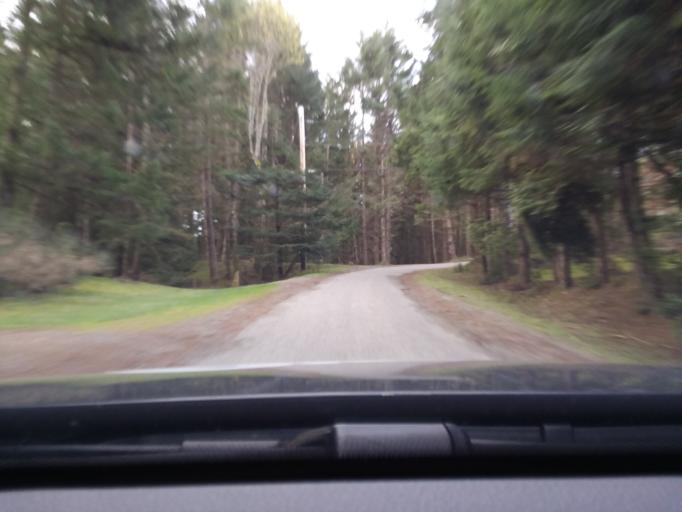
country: CA
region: British Columbia
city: North Saanich
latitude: 48.8746
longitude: -123.3262
